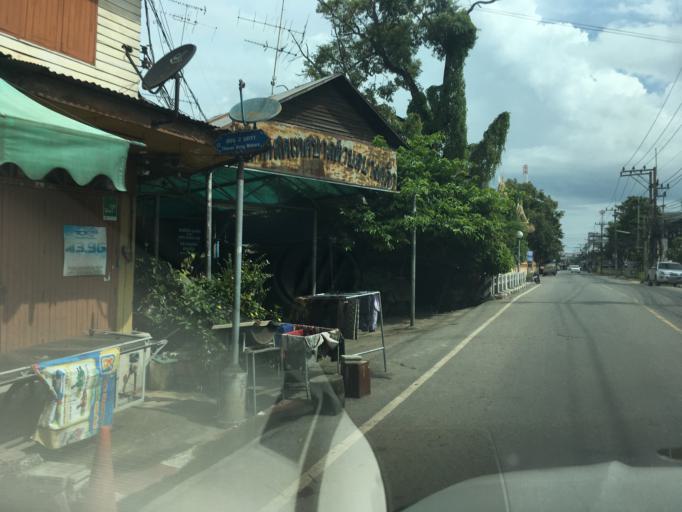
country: TH
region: Chachoengsao
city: Bang Khla
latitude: 13.7251
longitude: 101.2063
